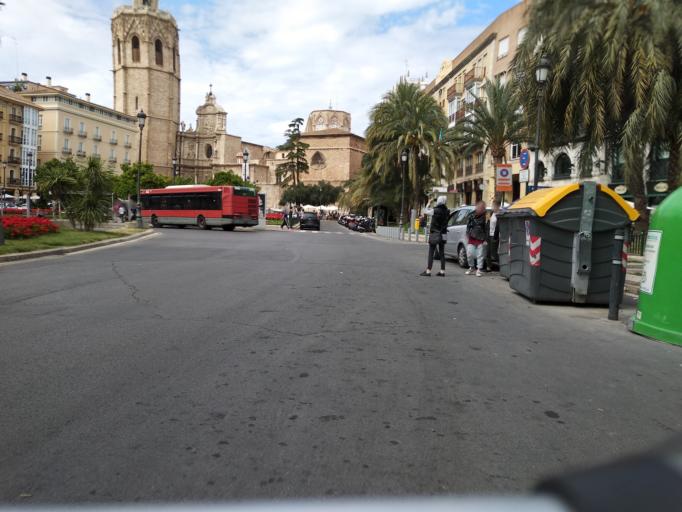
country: ES
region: Valencia
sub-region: Provincia de Valencia
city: Valencia
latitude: 39.4740
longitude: -0.3754
